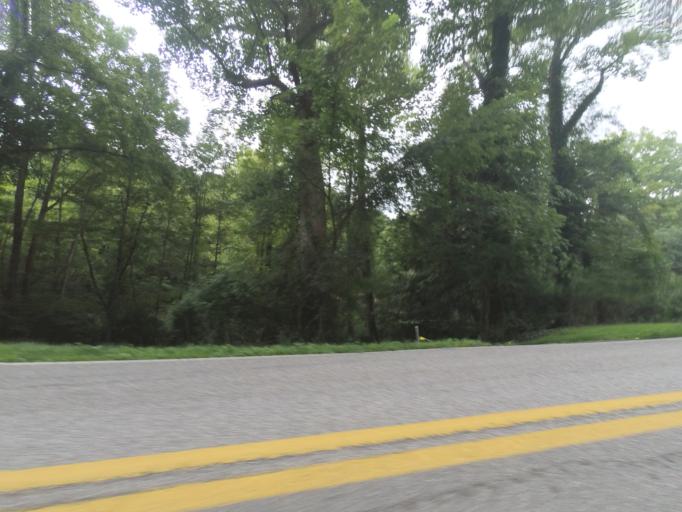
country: US
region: West Virginia
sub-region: Cabell County
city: Huntington
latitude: 38.3941
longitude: -82.4447
